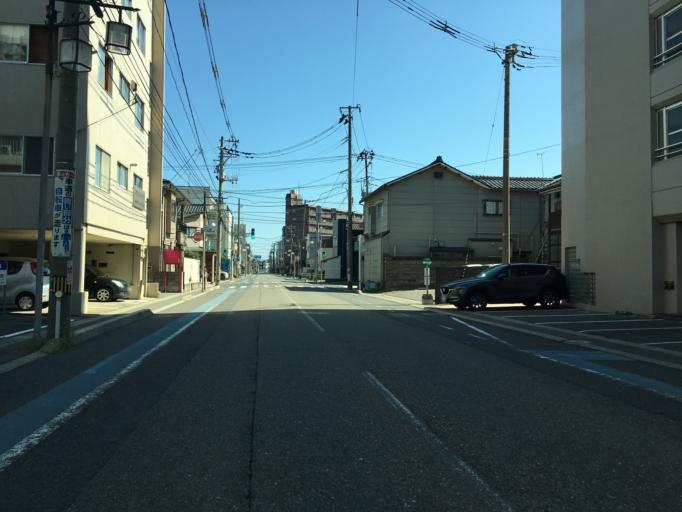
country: JP
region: Niigata
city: Niigata-shi
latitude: 37.9061
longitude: 139.0086
